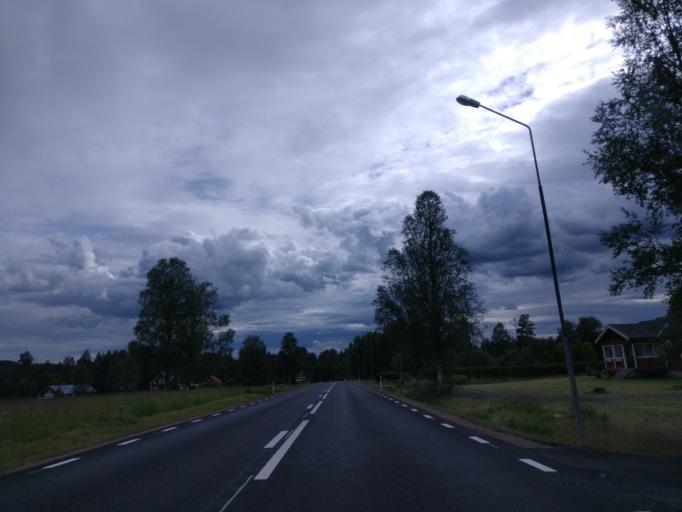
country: SE
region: Vaermland
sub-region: Hagfors Kommun
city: Ekshaerad
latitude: 60.0714
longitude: 13.5516
